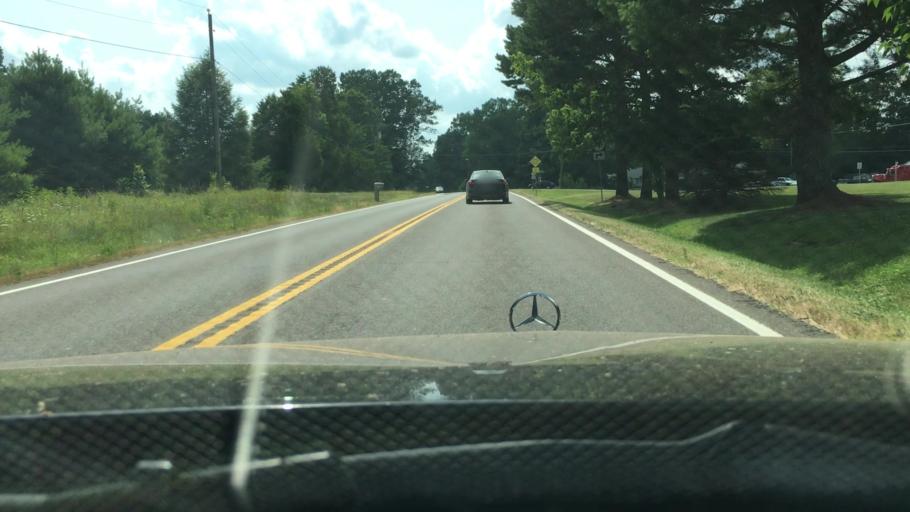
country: US
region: Virginia
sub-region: Orange County
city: Orange
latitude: 38.2691
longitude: -77.9440
